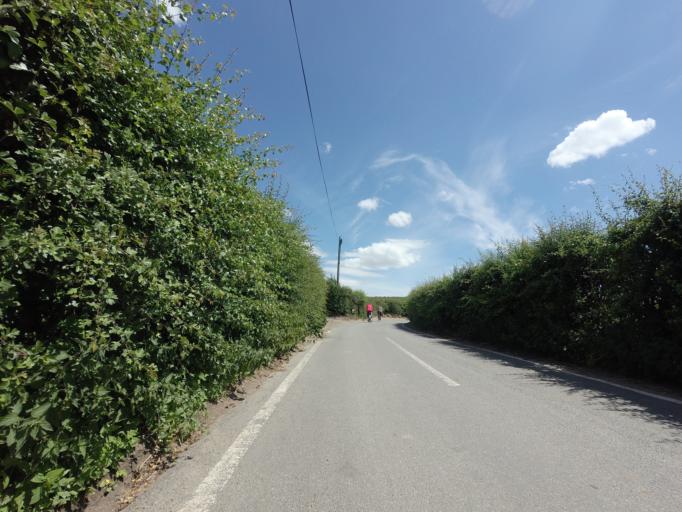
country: GB
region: England
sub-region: Medway
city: Cooling
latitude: 51.4564
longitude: 0.5394
